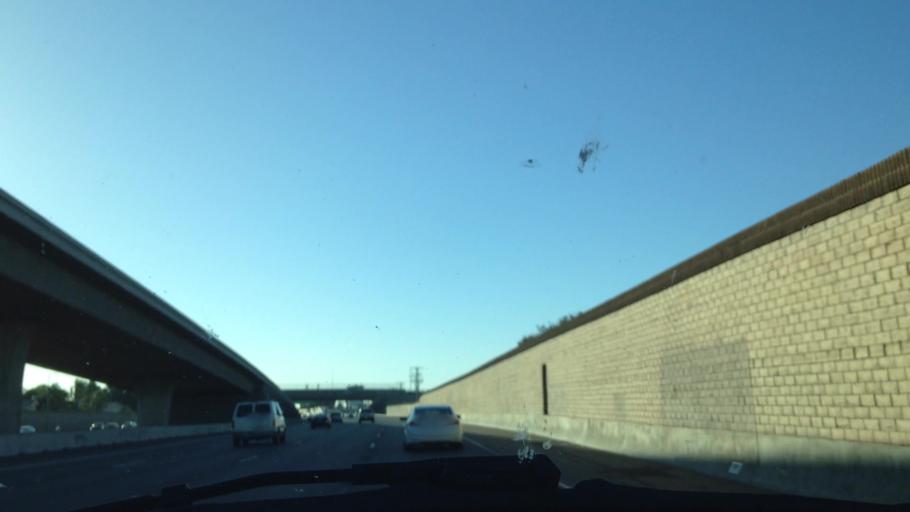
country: US
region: California
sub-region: Orange County
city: Placentia
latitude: 33.8527
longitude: -117.8811
